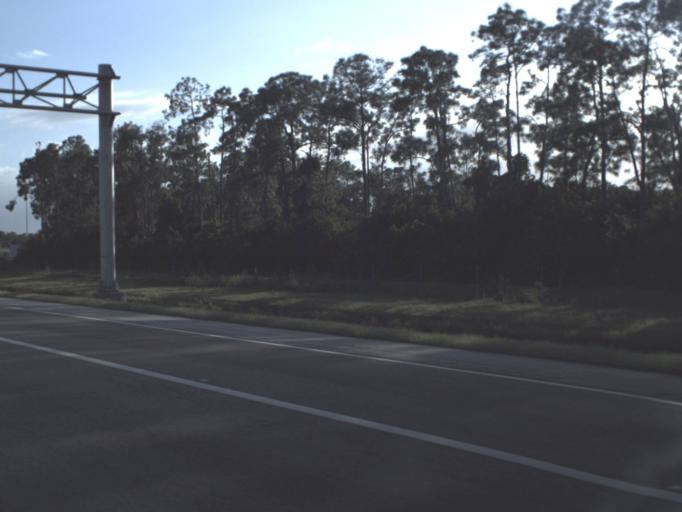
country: US
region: Florida
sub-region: Lee County
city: Three Oaks
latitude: 26.4996
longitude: -81.7950
